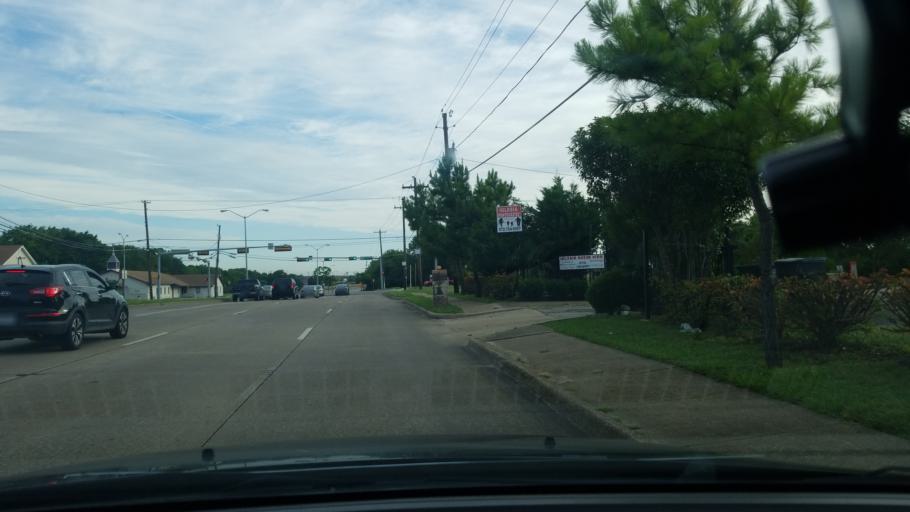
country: US
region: Texas
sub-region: Dallas County
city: Balch Springs
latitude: 32.7614
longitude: -96.6480
